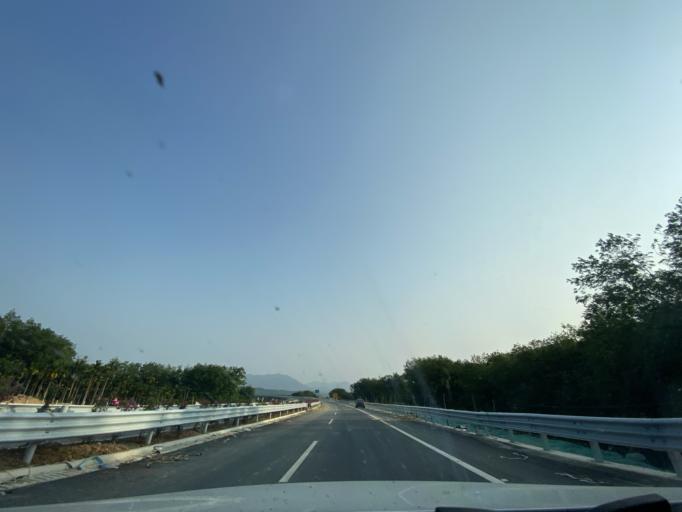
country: CN
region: Hainan
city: Xiangshui
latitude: 18.6423
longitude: 109.6291
